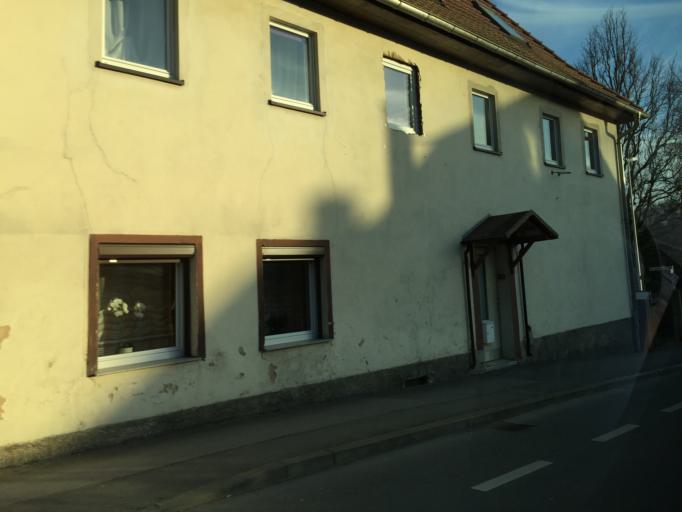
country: DE
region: Saxony
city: Lobau
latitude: 51.0918
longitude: 14.6747
